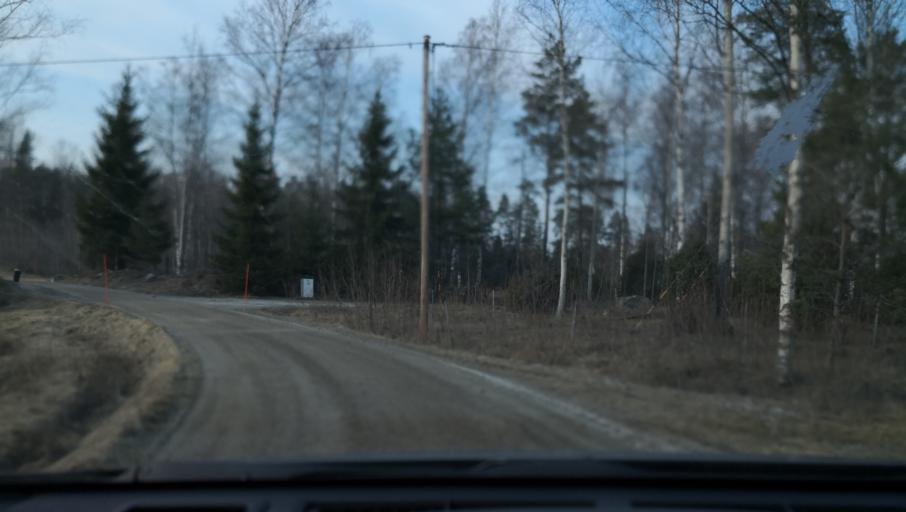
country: SE
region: OErebro
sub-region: Lindesbergs Kommun
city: Frovi
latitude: 59.3859
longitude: 15.3626
